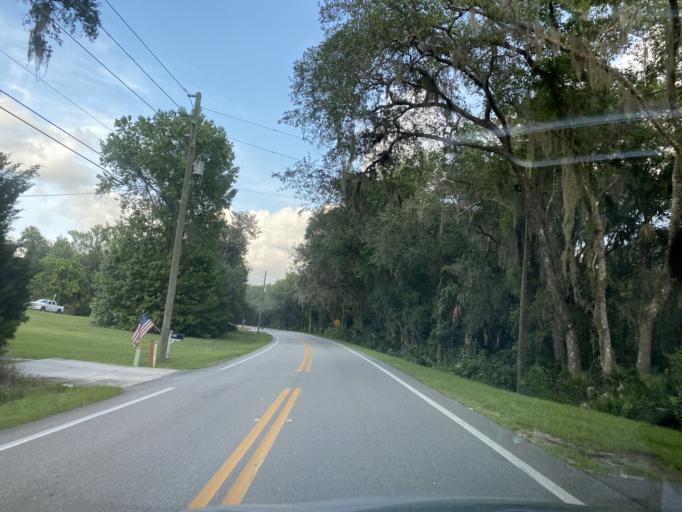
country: US
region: Florida
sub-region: Volusia County
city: DeBary
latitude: 28.8676
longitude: -81.2996
